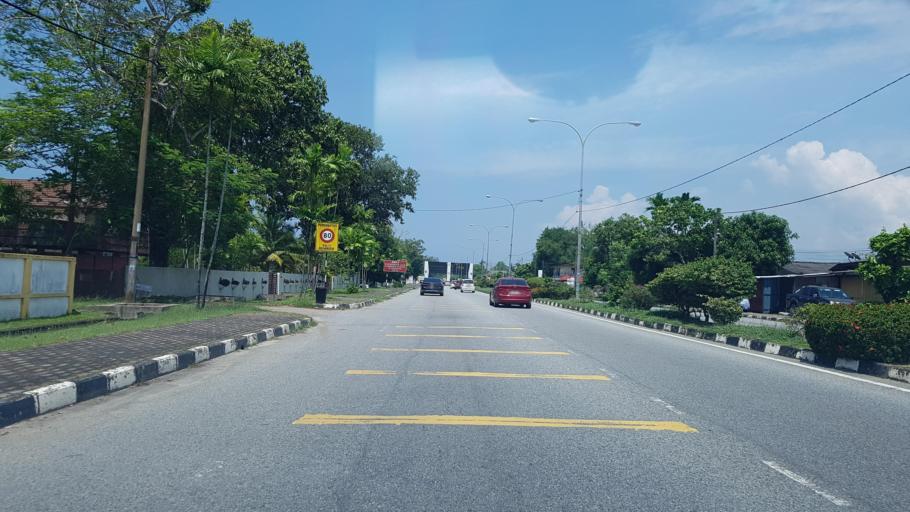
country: MY
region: Terengganu
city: Kuala Terengganu
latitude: 5.3081
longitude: 103.1582
